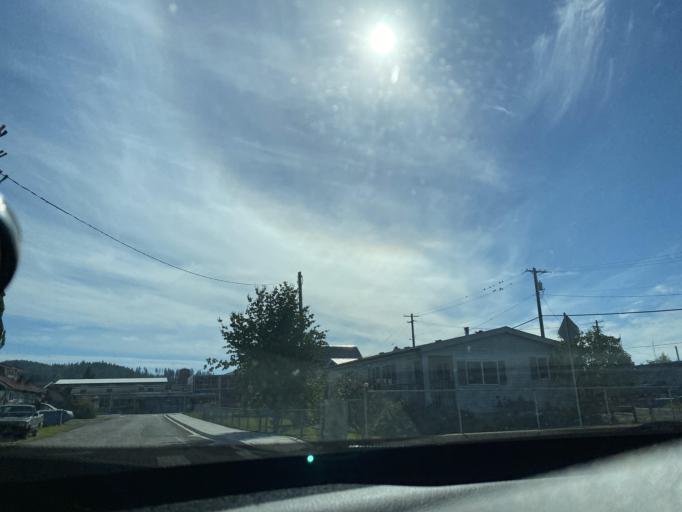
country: US
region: Washington
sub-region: Clallam County
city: Forks
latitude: 47.9505
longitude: -124.3832
